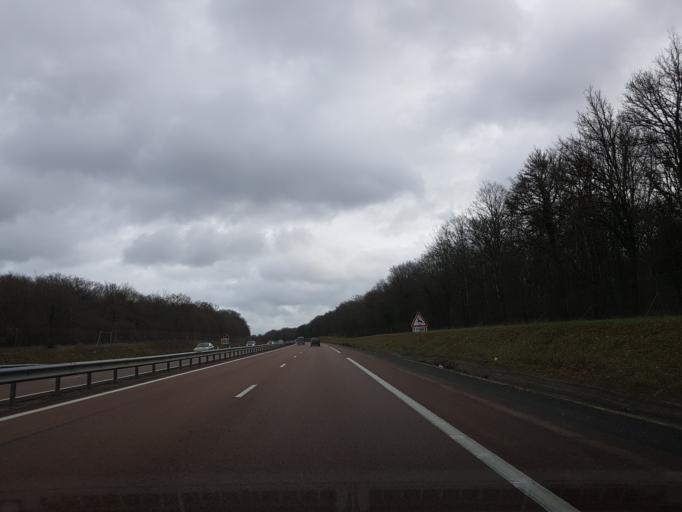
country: FR
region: Champagne-Ardenne
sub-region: Departement de la Haute-Marne
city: Chateauvillain
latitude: 48.0423
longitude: 4.9910
